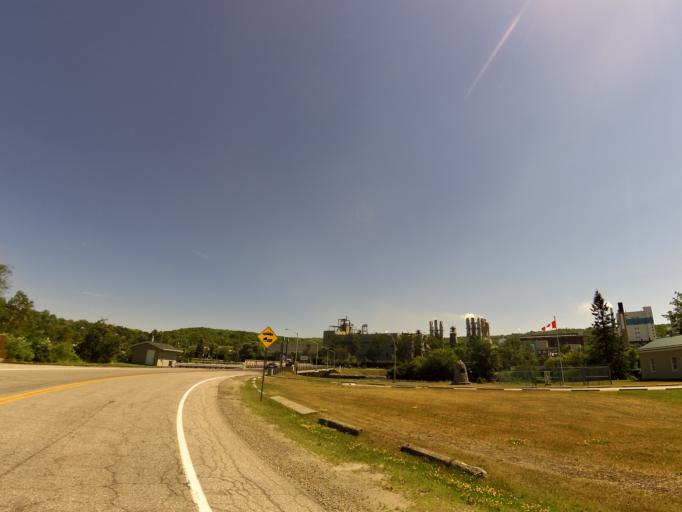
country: CA
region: Quebec
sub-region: Abitibi-Temiscamingue
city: Temiscaming
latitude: 46.7110
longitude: -79.1017
